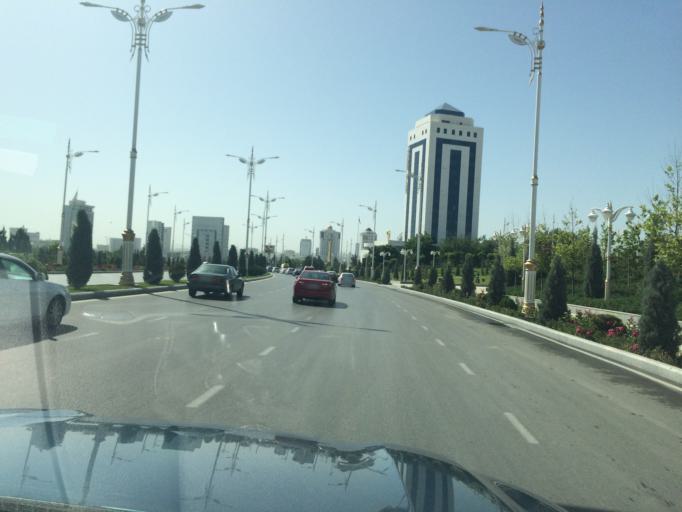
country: TM
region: Ahal
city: Ashgabat
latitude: 37.9286
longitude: 58.3698
